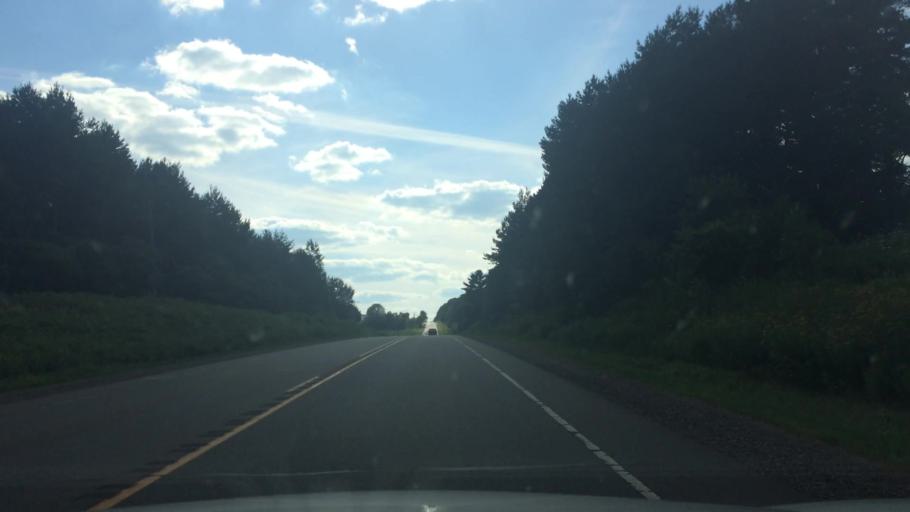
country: US
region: Wisconsin
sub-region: Lincoln County
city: Merrill
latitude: 45.1780
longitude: -89.5997
